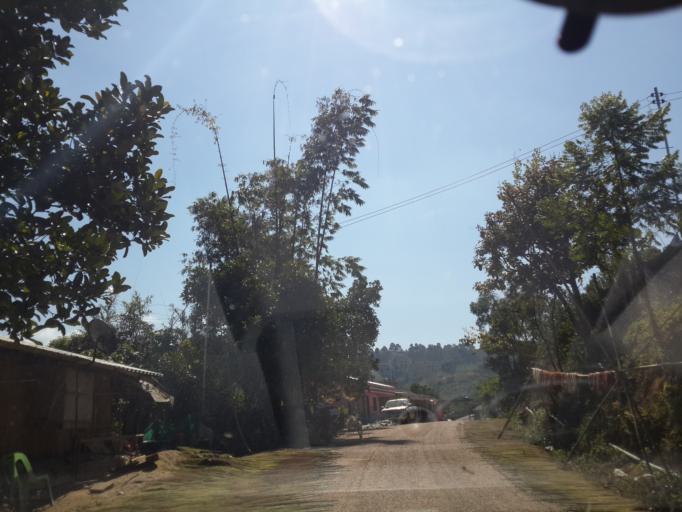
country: TH
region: Chiang Mai
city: Fang
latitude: 19.9396
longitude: 99.0421
